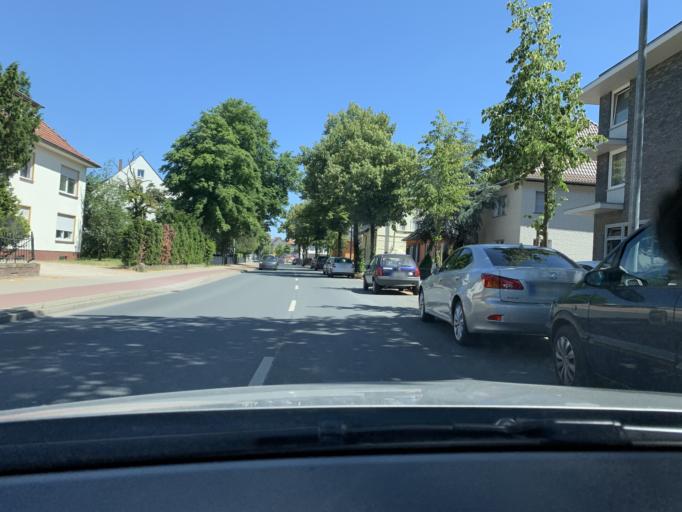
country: DE
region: North Rhine-Westphalia
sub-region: Regierungsbezirk Detmold
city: Rheda-Wiedenbruck
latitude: 51.8556
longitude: 8.2888
